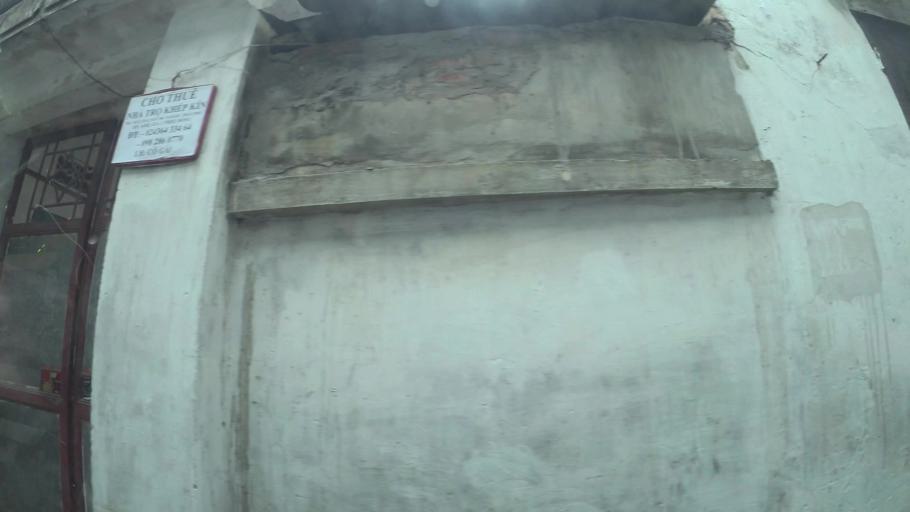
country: VN
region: Ha Noi
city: Van Dien
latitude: 20.9772
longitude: 105.8853
